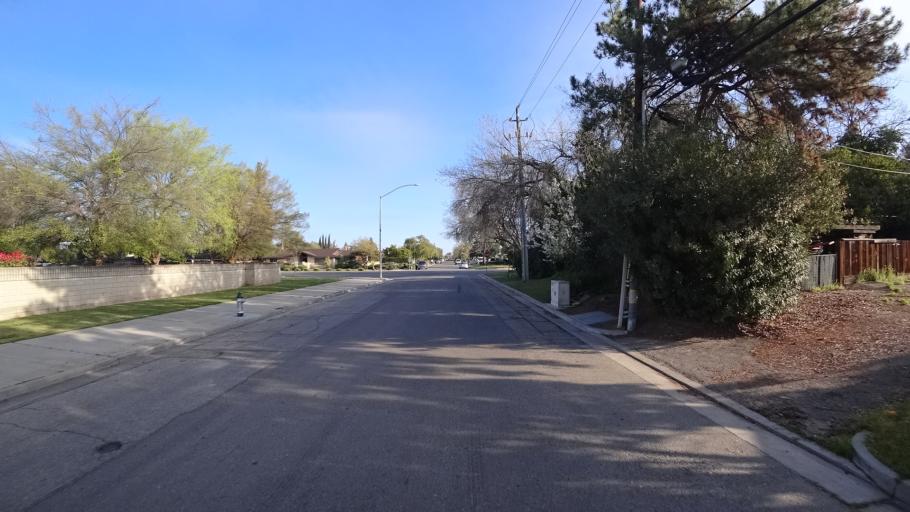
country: US
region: California
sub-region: Fresno County
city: Fresno
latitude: 36.8224
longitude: -119.7948
